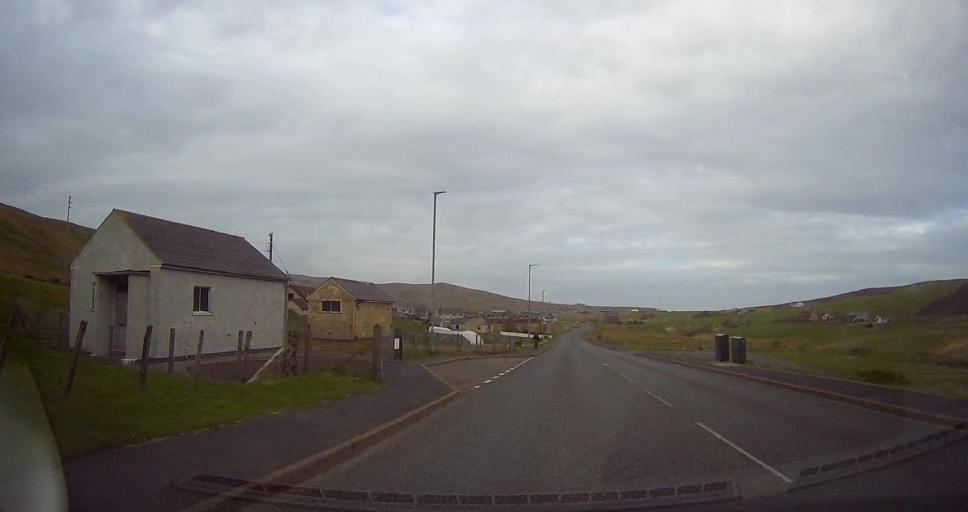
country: GB
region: Scotland
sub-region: Shetland Islands
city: Sandwick
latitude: 60.0496
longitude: -1.2274
